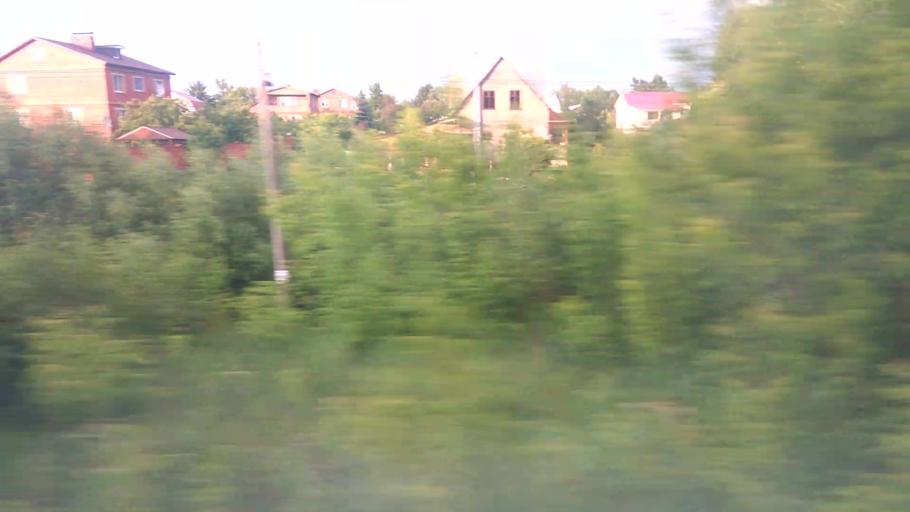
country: RU
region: Moskovskaya
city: Stupino
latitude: 54.8937
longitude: 38.0937
